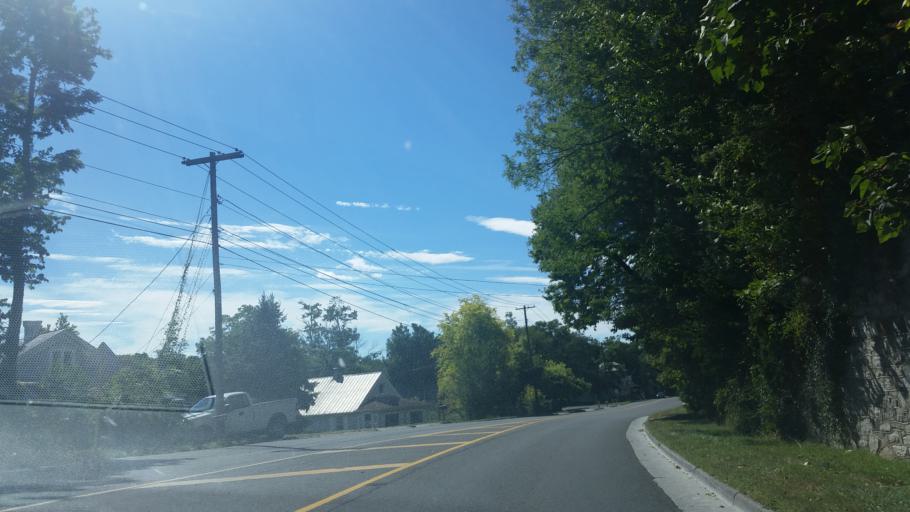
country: US
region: Virginia
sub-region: City of Winchester
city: Winchester
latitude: 39.2005
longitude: -78.1642
